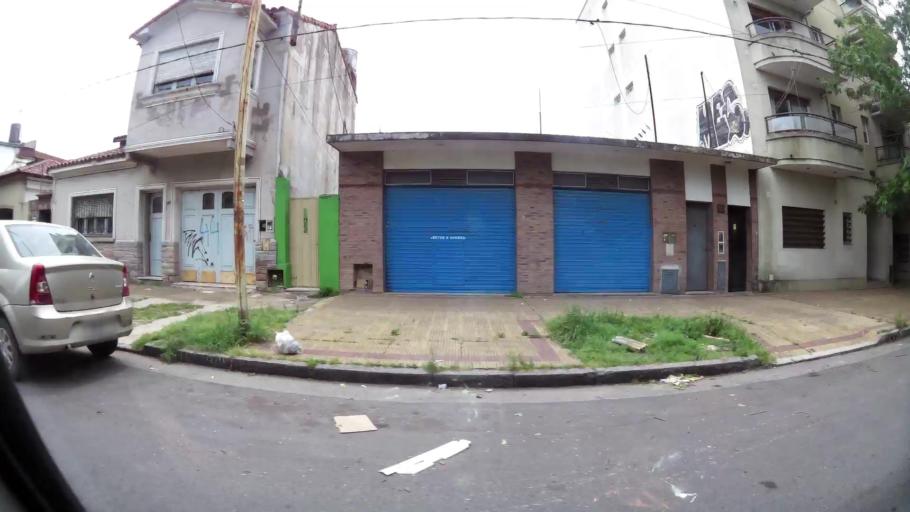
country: AR
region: Buenos Aires
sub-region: Partido de La Plata
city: La Plata
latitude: -34.9409
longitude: -57.9635
